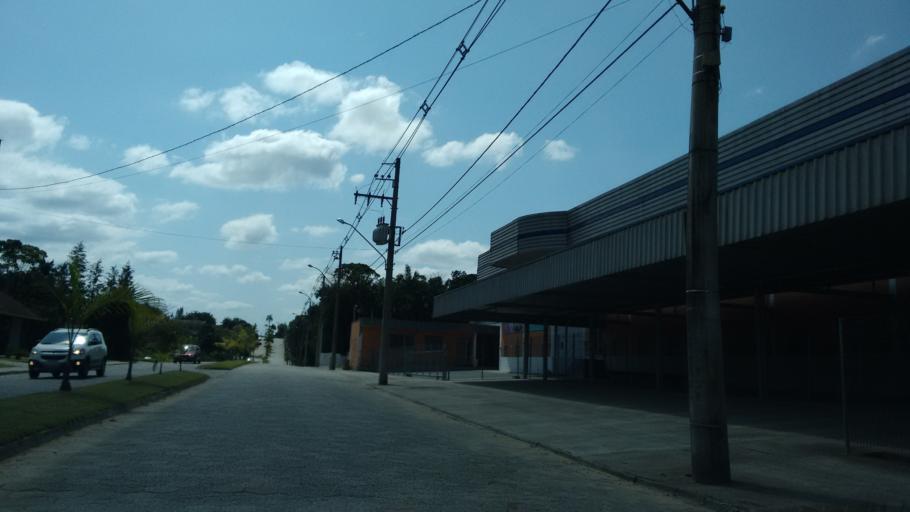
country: BR
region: Santa Catarina
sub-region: Pomerode
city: Pomerode
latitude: -26.7530
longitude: -49.1748
